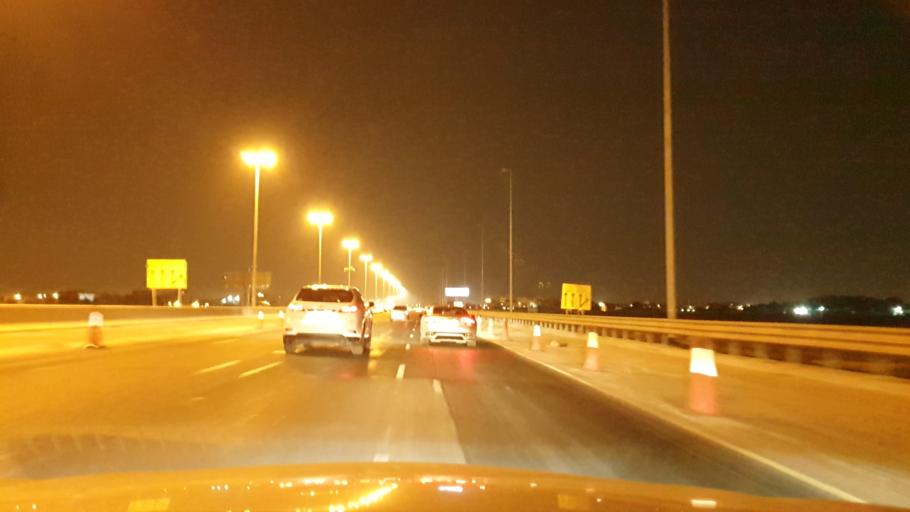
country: BH
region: Manama
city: Jidd Hafs
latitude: 26.2042
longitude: 50.5135
